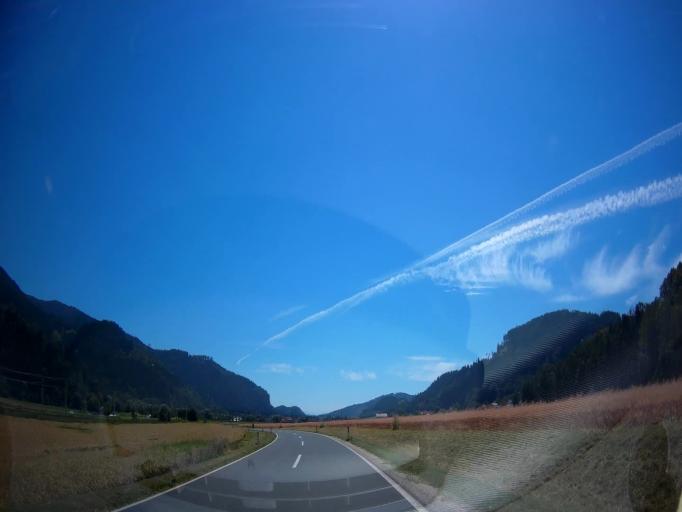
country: AT
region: Carinthia
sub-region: Politischer Bezirk Sankt Veit an der Glan
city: Micheldorf
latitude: 46.9221
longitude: 14.4281
